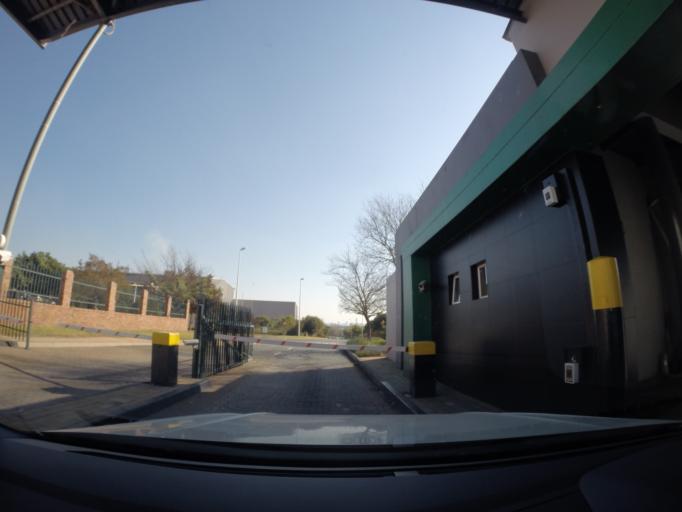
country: ZA
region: Gauteng
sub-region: City of Johannesburg Metropolitan Municipality
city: Modderfontein
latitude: -26.0912
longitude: 28.1226
